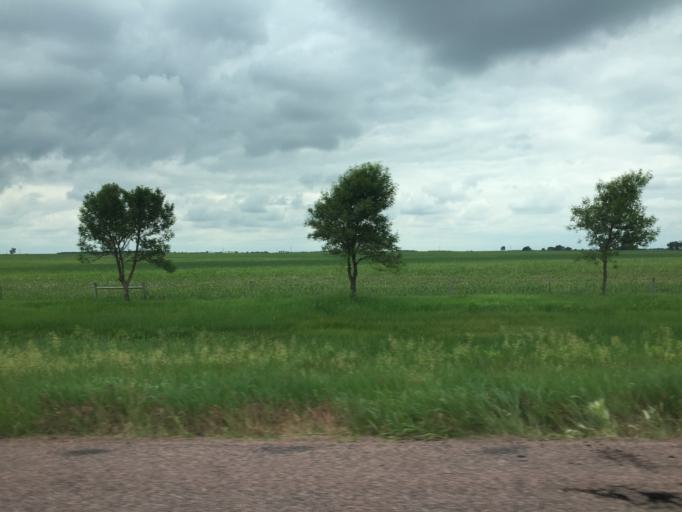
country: US
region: South Dakota
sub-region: Hanson County
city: Alexandria
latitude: 43.6657
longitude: -97.7218
